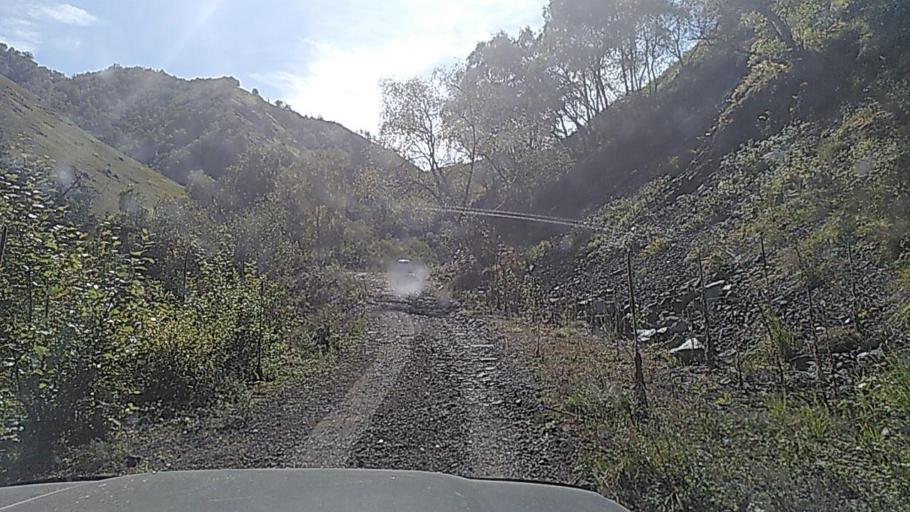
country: RU
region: Kabardino-Balkariya
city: Kamennomostskoye
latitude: 43.7182
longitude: 42.8442
